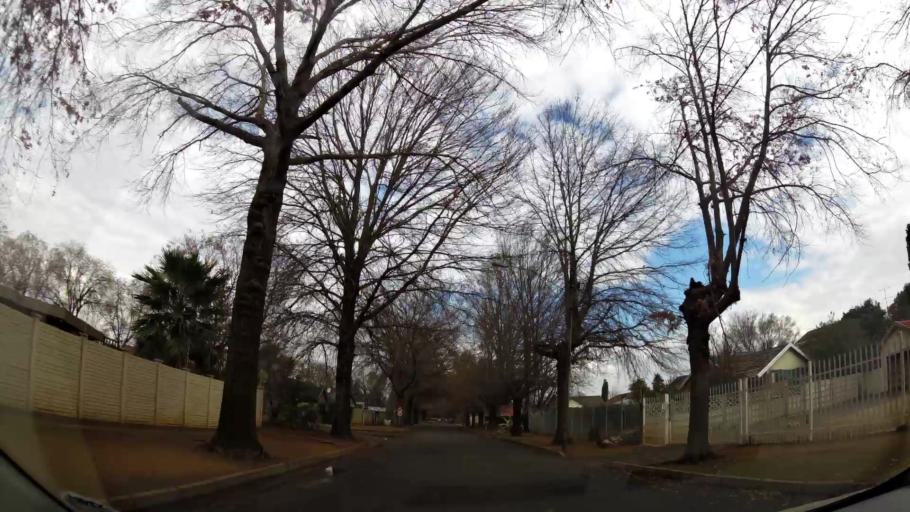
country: ZA
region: Gauteng
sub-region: Sedibeng District Municipality
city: Vereeniging
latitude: -26.6427
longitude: 27.9744
